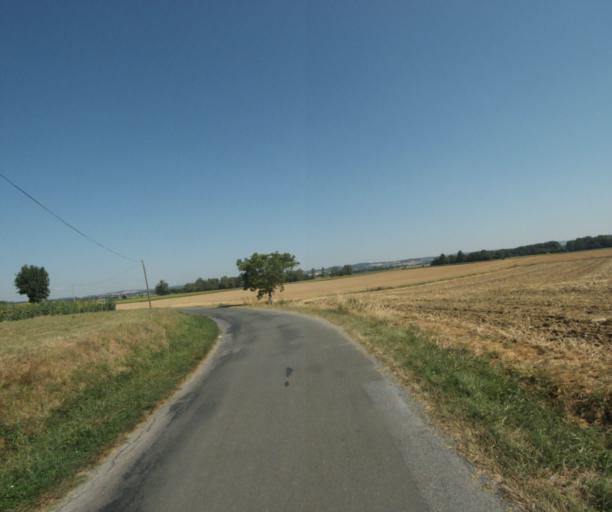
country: FR
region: Midi-Pyrenees
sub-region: Departement de la Haute-Garonne
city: Revel
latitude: 43.5127
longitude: 1.9502
